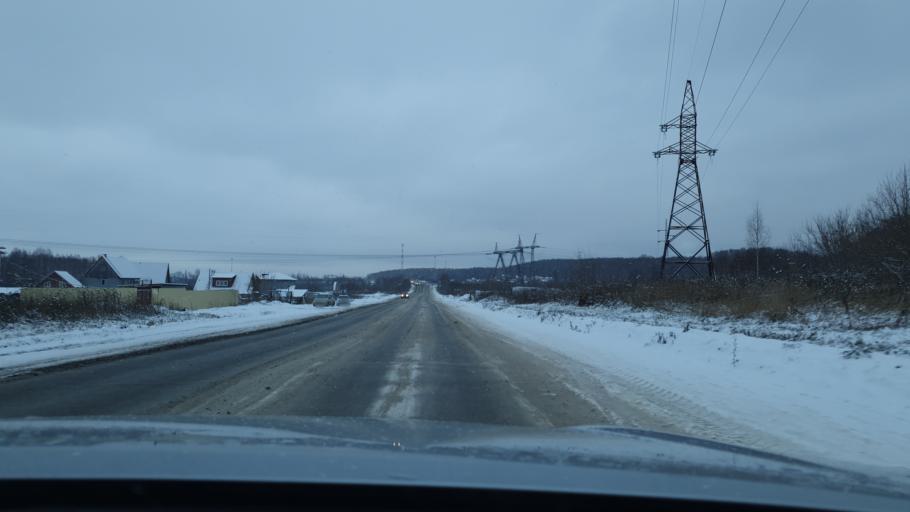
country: RU
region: Sverdlovsk
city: Istok
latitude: 56.7756
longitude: 60.7388
